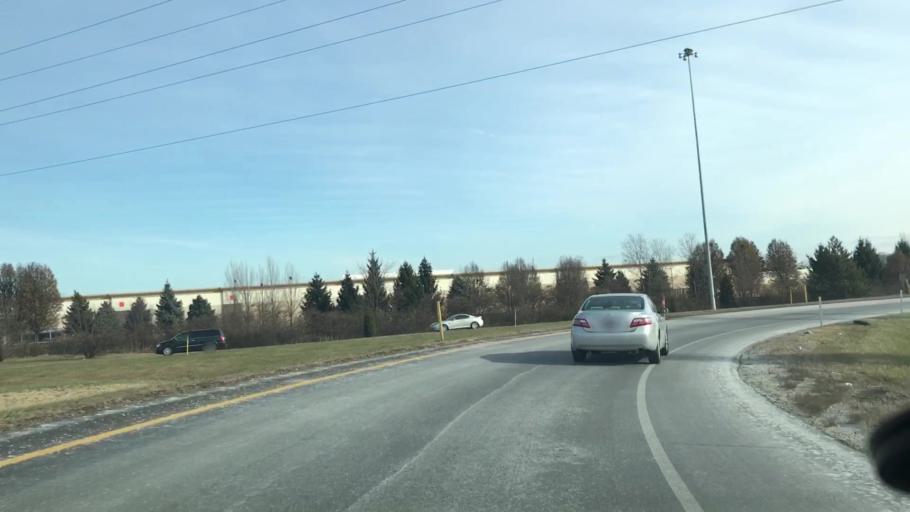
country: US
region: Ohio
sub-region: Franklin County
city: Hilliard
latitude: 40.0347
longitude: -83.1233
